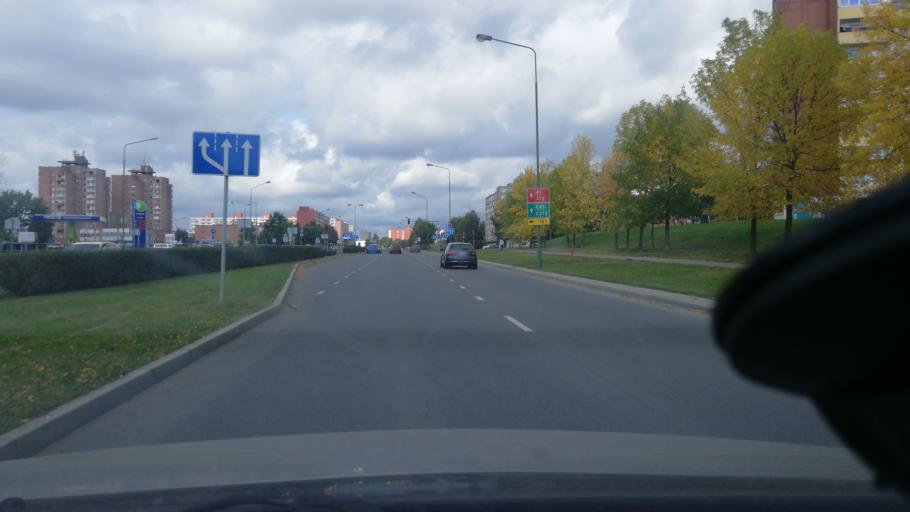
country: LT
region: Klaipedos apskritis
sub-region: Klaipeda
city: Klaipeda
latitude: 55.6693
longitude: 21.1944
